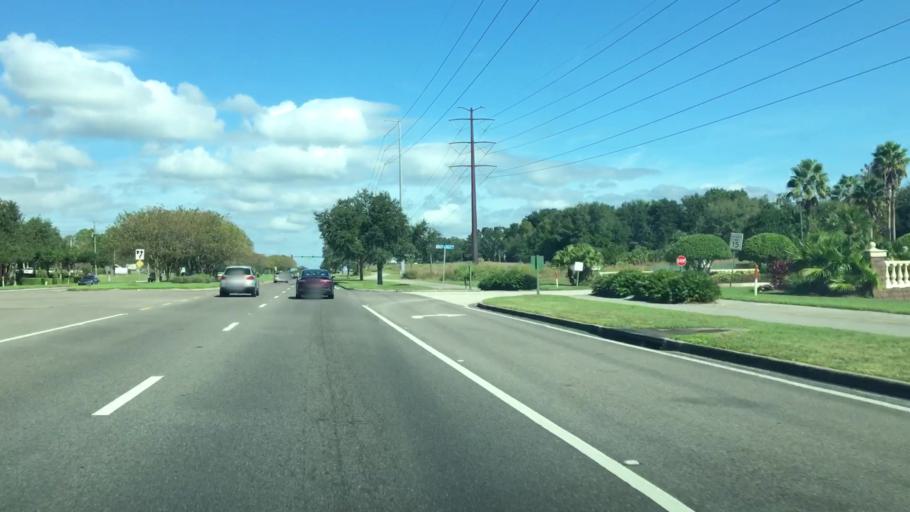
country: US
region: Florida
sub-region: Seminole County
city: Heathrow
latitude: 28.7767
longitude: -81.3471
